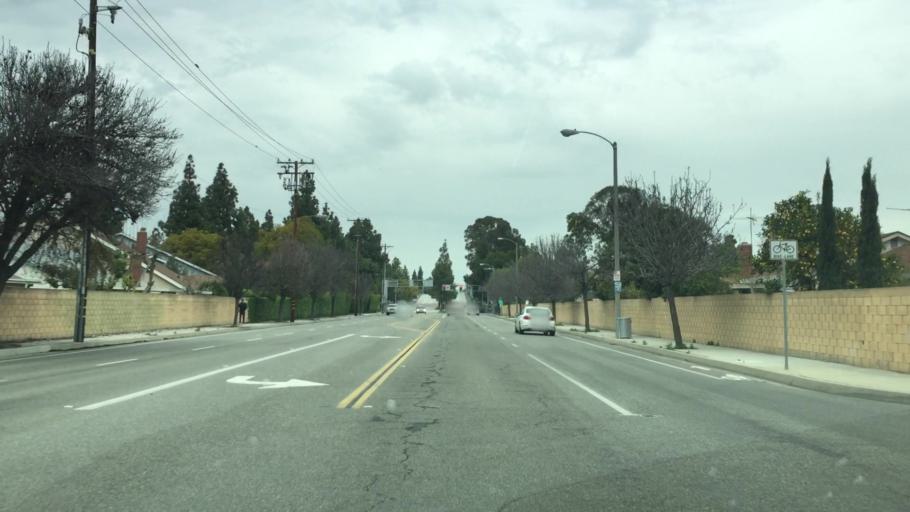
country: US
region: California
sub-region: Los Angeles County
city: Cerritos
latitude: 33.8641
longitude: -118.0550
